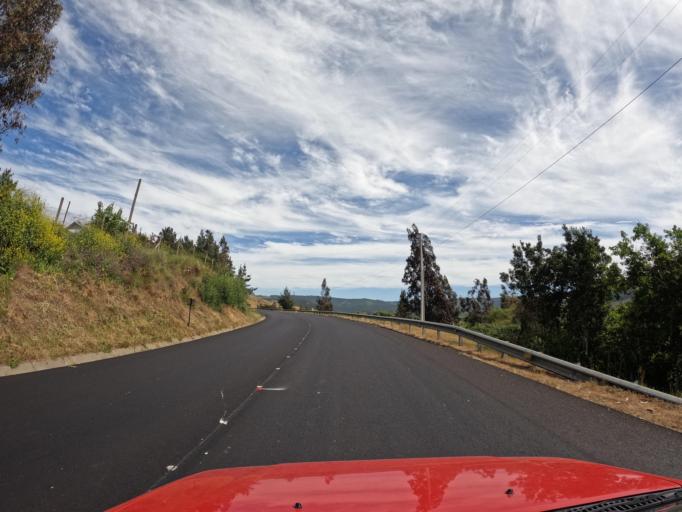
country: CL
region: Maule
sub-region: Provincia de Talca
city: Constitucion
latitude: -35.0653
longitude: -72.0390
